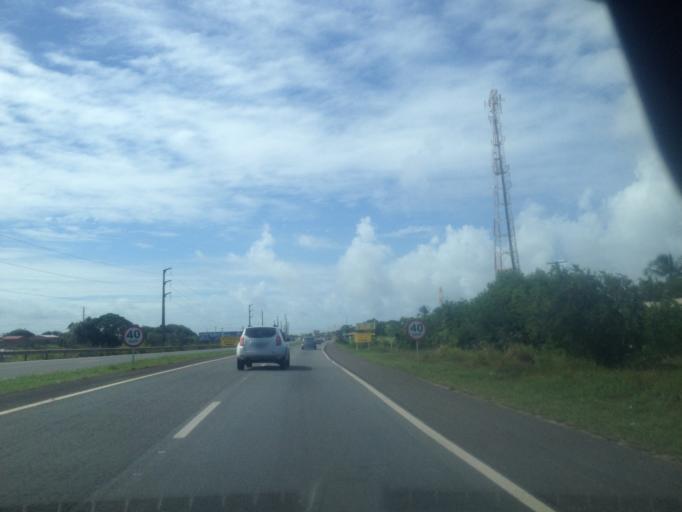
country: BR
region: Bahia
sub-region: Camacari
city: Camacari
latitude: -12.6501
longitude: -38.0826
